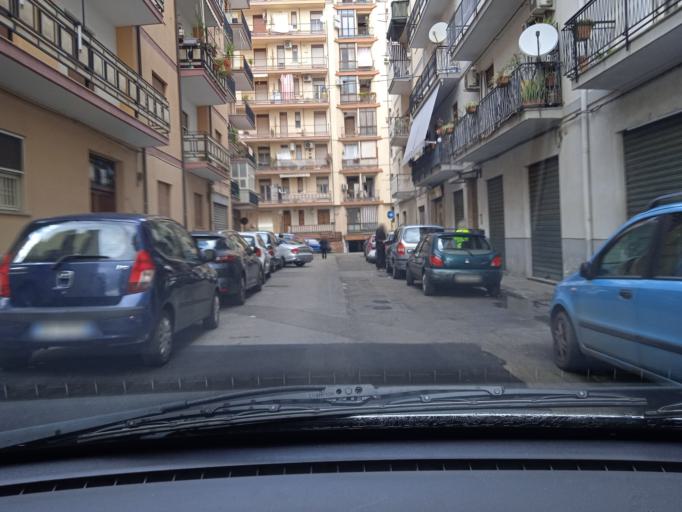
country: IT
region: Sicily
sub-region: Palermo
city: Palermo
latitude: 38.1060
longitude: 13.3420
